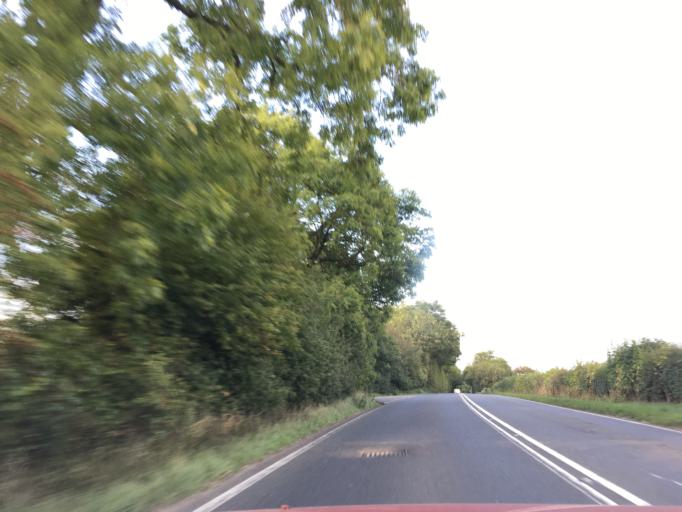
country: GB
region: England
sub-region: Gloucestershire
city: Bourton on the Water
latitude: 51.8698
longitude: -1.7915
